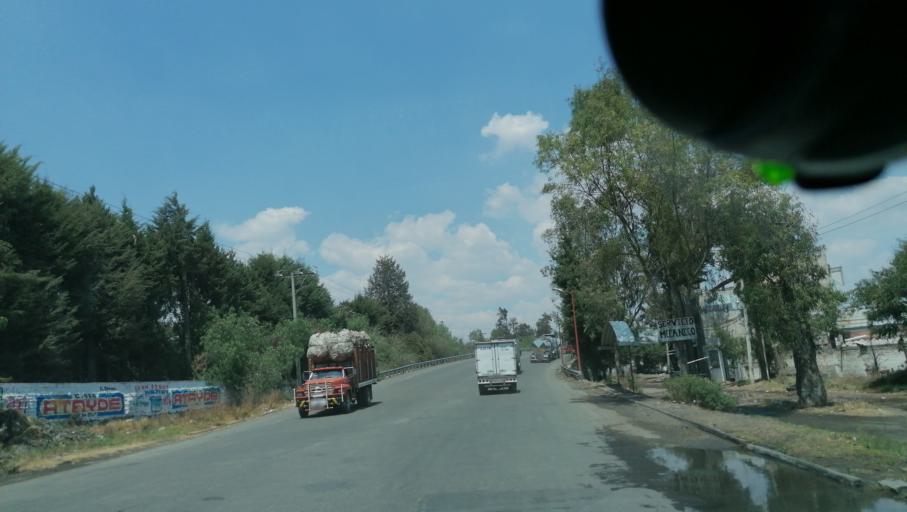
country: MX
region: Puebla
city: San Martin Texmelucan de Labastida
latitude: 19.2701
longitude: -98.4319
